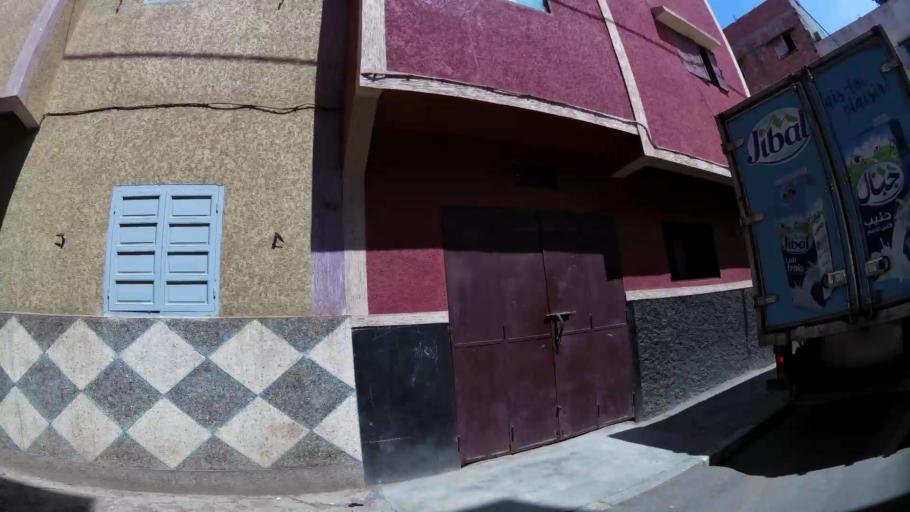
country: MA
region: Rabat-Sale-Zemmour-Zaer
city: Sale
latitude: 34.0656
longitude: -6.7838
